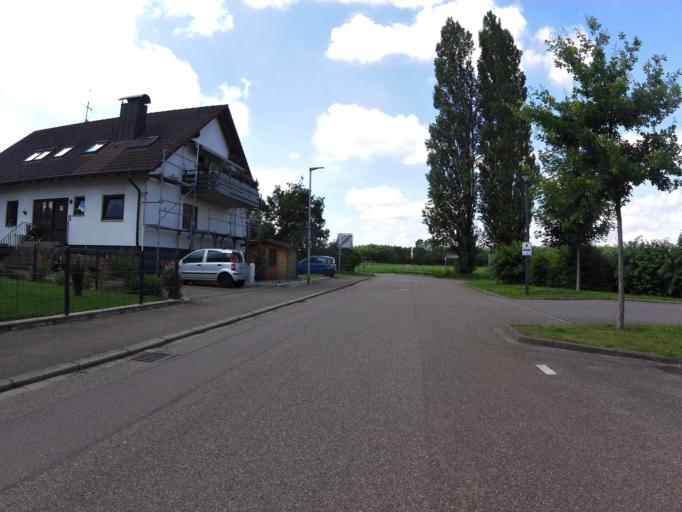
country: DE
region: Baden-Wuerttemberg
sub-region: Freiburg Region
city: Kippenheim
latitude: 48.3304
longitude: 7.8170
